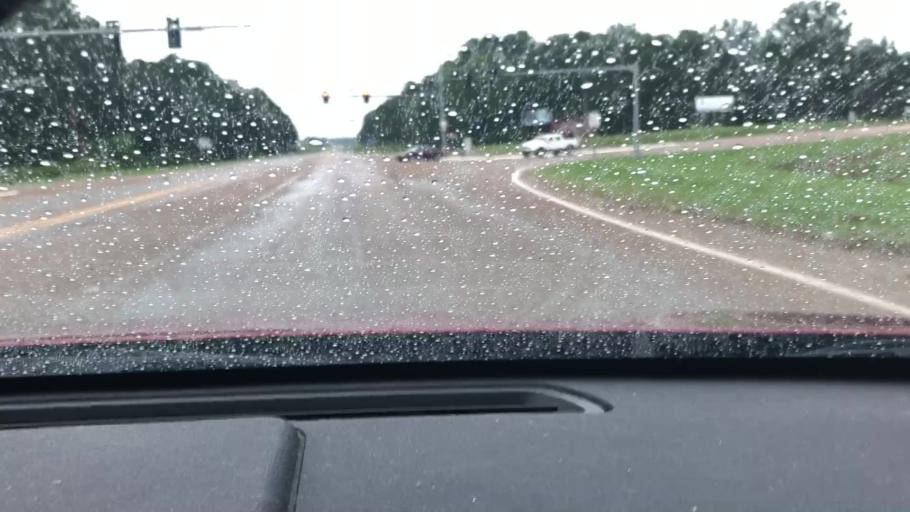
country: US
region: Arkansas
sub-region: Columbia County
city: Magnolia
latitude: 33.2965
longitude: -93.2508
